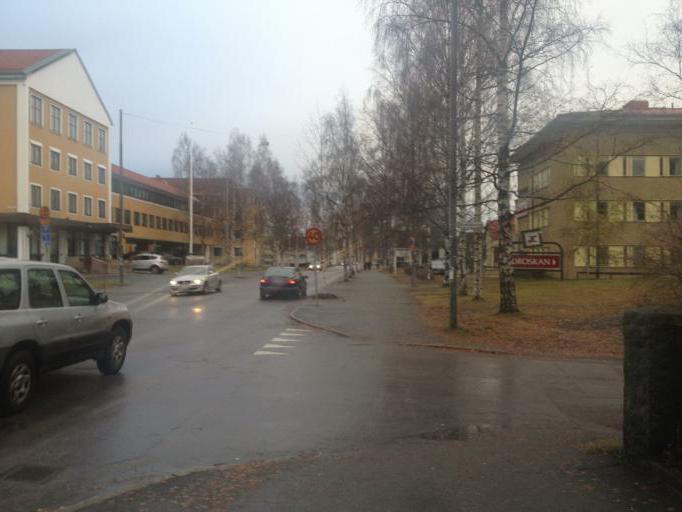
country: SE
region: Vaesterbotten
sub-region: Umea Kommun
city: Umea
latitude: 63.8230
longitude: 20.2740
